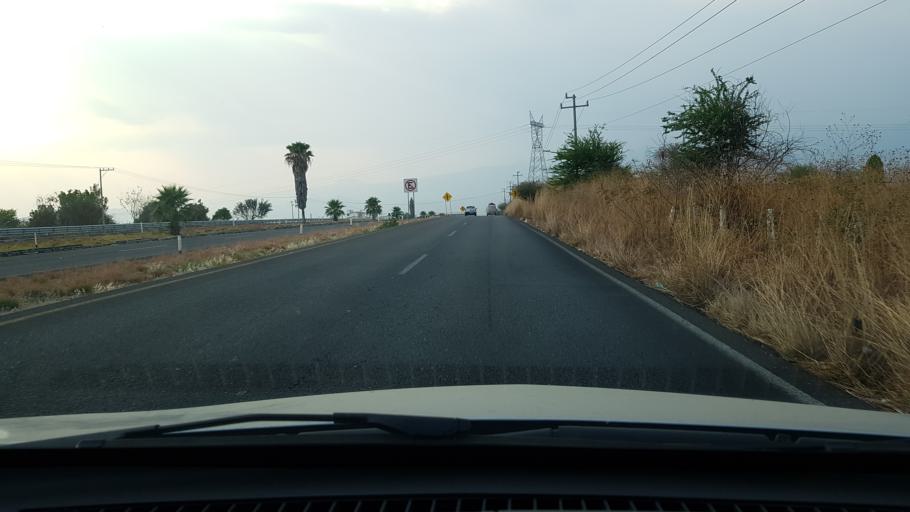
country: MX
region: Morelos
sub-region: Cuautla
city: Narciso Mendoza
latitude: 18.8755
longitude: -98.9591
